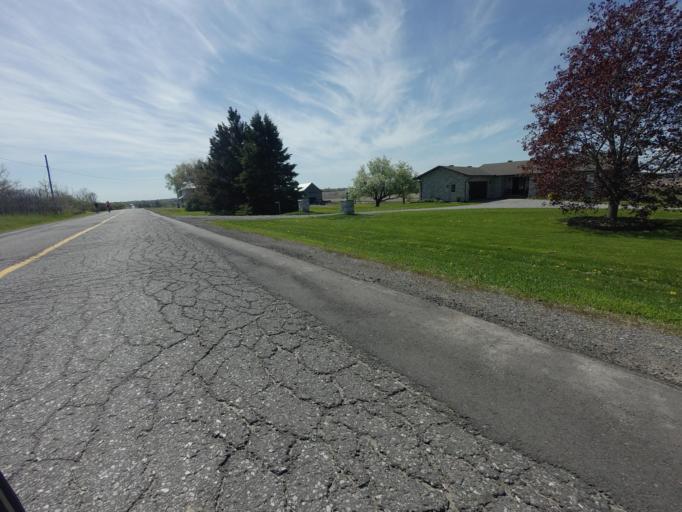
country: CA
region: Ontario
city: Arnprior
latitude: 45.3787
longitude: -76.1250
